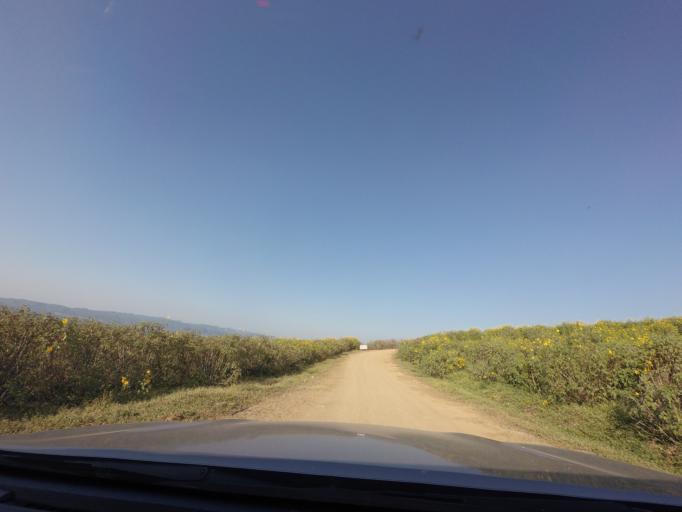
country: TH
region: Lampang
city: Mae Mo
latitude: 18.3497
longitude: 99.7548
